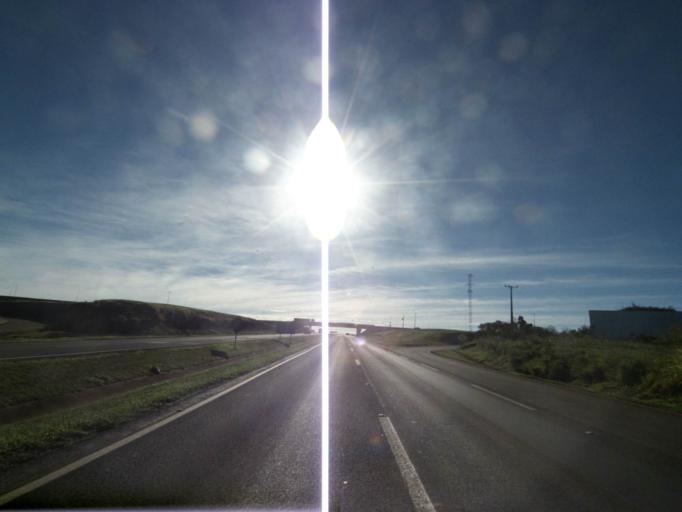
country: BR
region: Parana
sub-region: Cascavel
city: Cascavel
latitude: -25.0258
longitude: -53.5528
